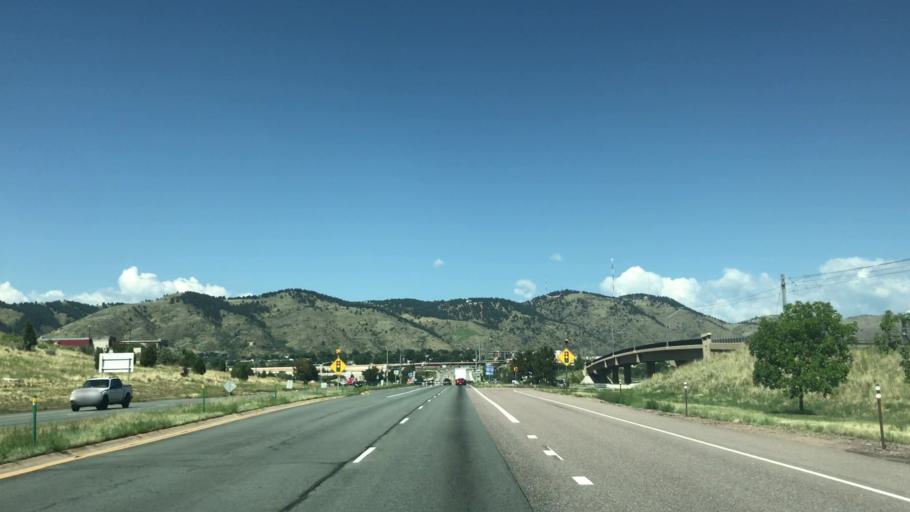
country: US
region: Colorado
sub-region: Jefferson County
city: West Pleasant View
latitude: 39.7254
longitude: -105.1857
